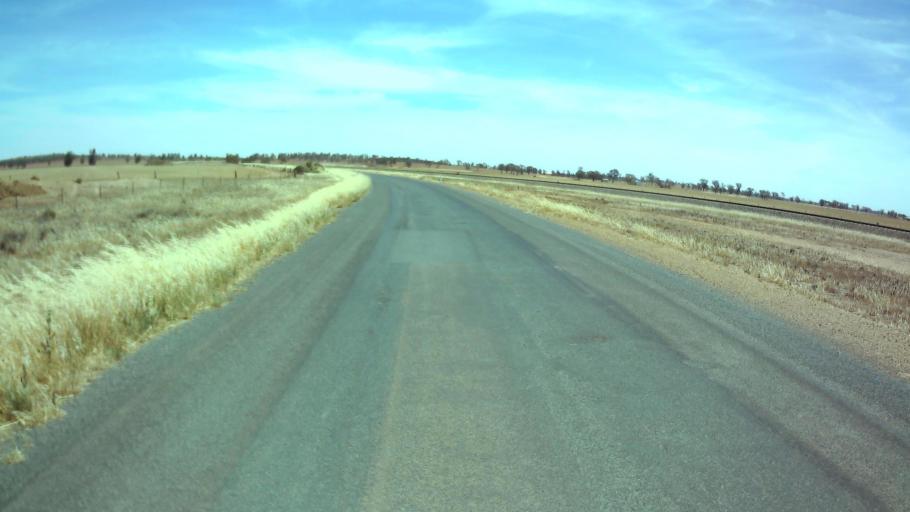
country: AU
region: New South Wales
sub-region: Weddin
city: Grenfell
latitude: -33.7545
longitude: 147.7639
